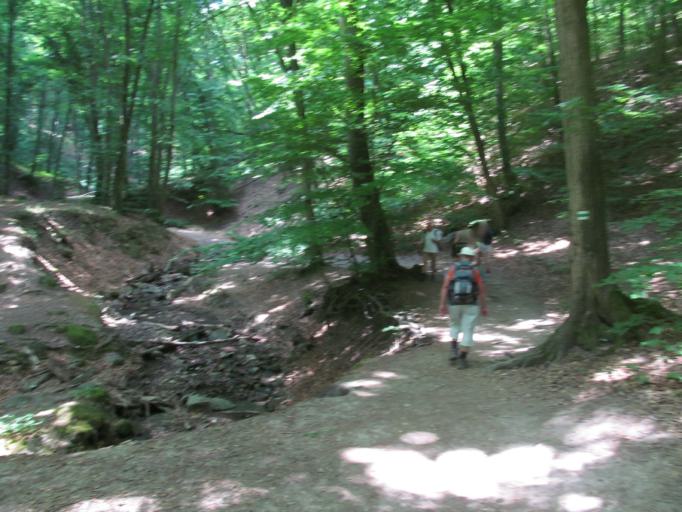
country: HU
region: Komarom-Esztergom
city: Pilismarot
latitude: 47.7441
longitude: 18.8987
